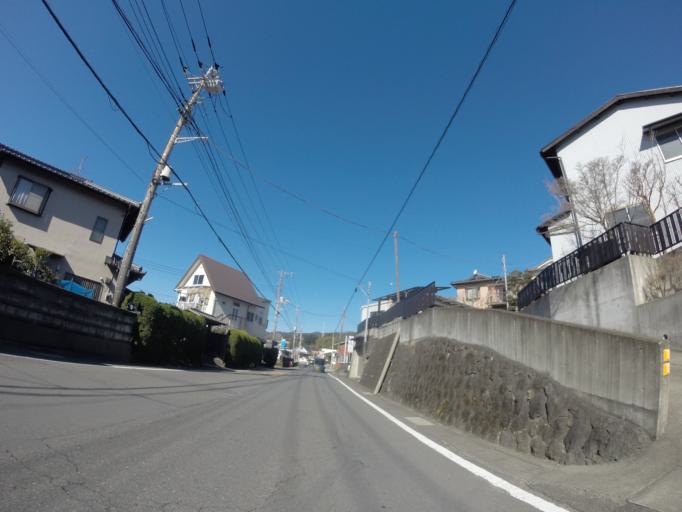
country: JP
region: Shizuoka
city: Numazu
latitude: 35.1441
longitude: 138.7922
